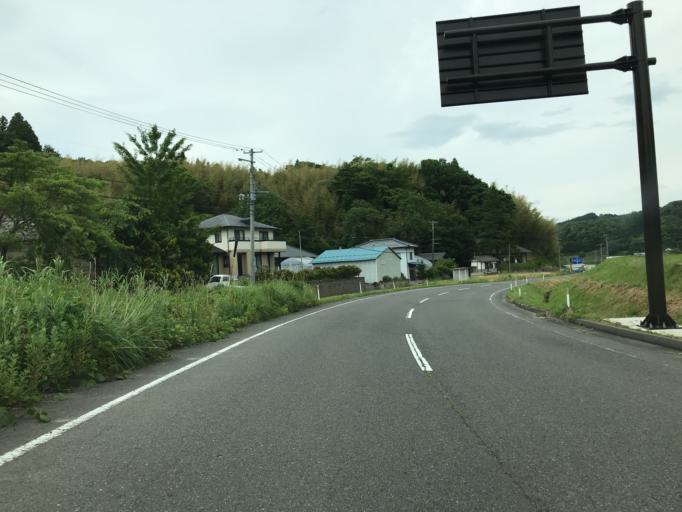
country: JP
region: Fukushima
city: Funehikimachi-funehiki
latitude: 37.4171
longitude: 140.6495
